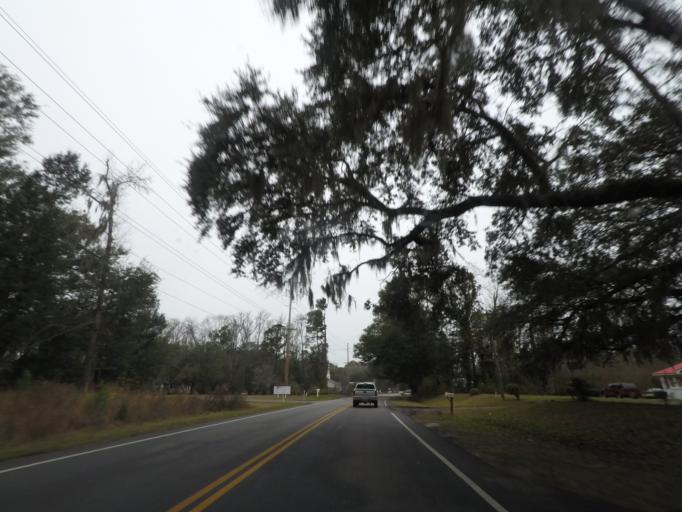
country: US
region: South Carolina
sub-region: Charleston County
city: Meggett
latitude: 32.5833
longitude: -80.3449
